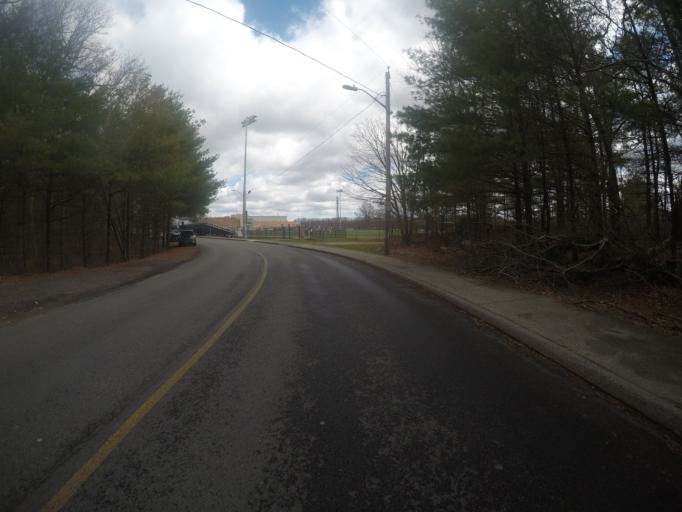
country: US
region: Massachusetts
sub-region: Bristol County
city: Easton
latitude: 42.0518
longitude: -71.1121
